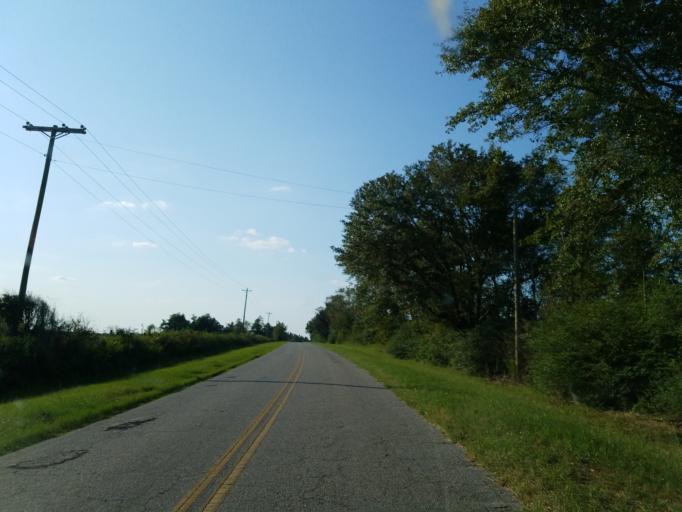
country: US
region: Georgia
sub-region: Cook County
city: Sparks
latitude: 31.2325
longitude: -83.4891
